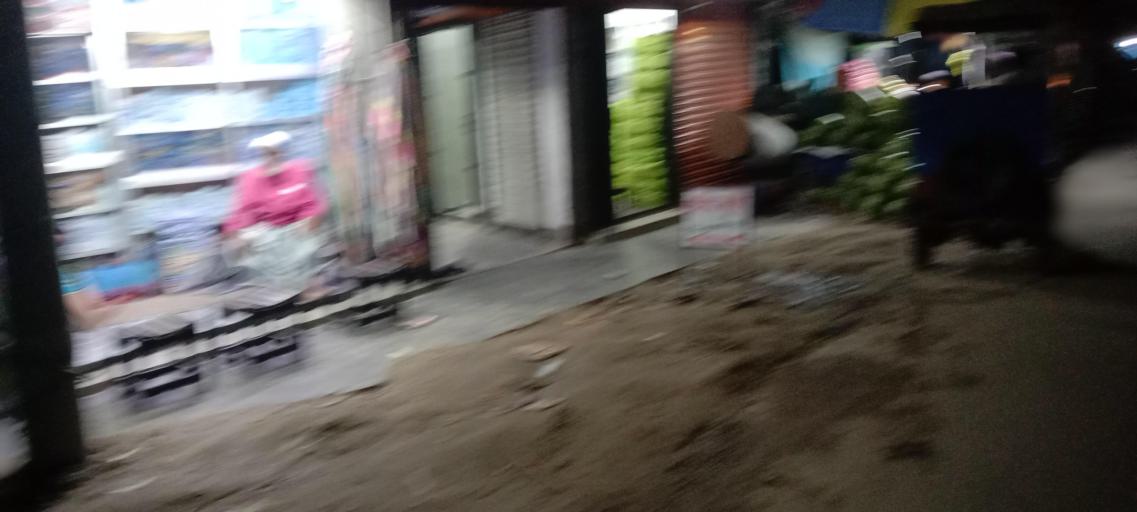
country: BD
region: Dhaka
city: Azimpur
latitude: 23.6910
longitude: 90.3089
